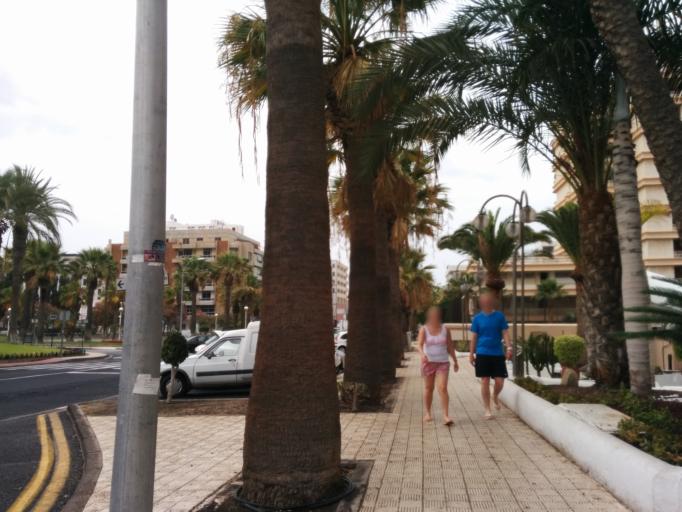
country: ES
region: Canary Islands
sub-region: Provincia de Santa Cruz de Tenerife
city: Playa de las Americas
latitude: 28.0599
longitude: -16.7290
